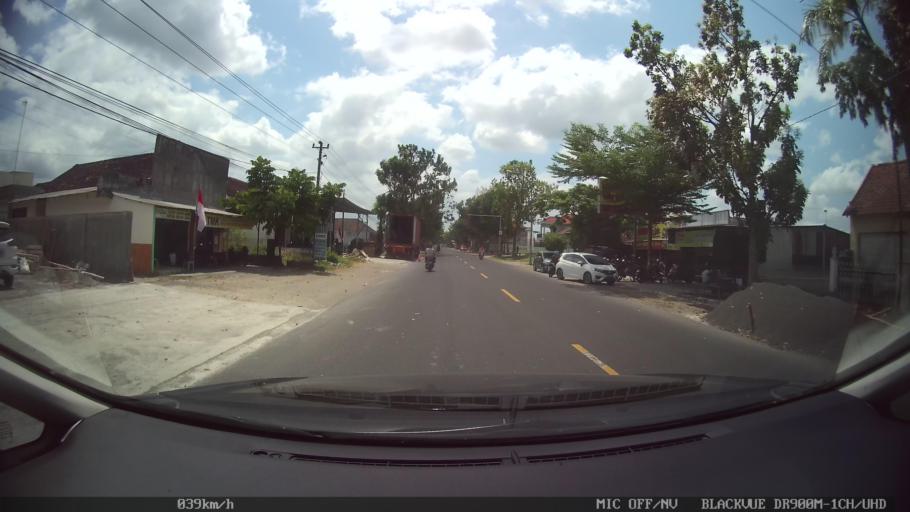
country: ID
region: Daerah Istimewa Yogyakarta
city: Bantul
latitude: -7.9044
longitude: 110.3453
